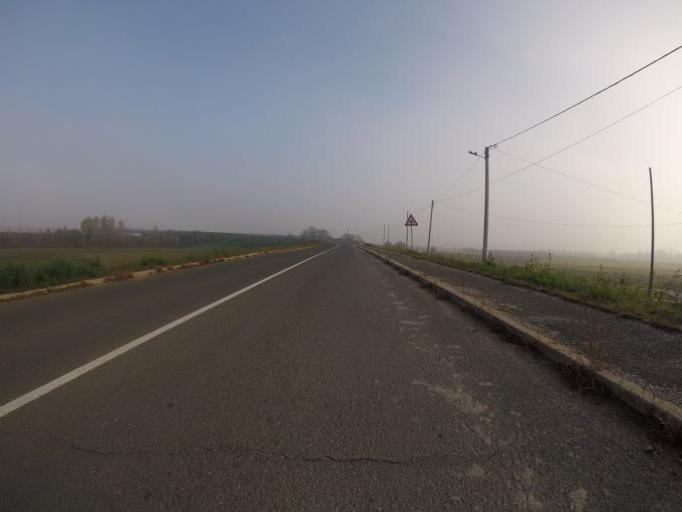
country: HR
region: Zagrebacka
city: Micevec
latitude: 45.7593
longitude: 16.0866
